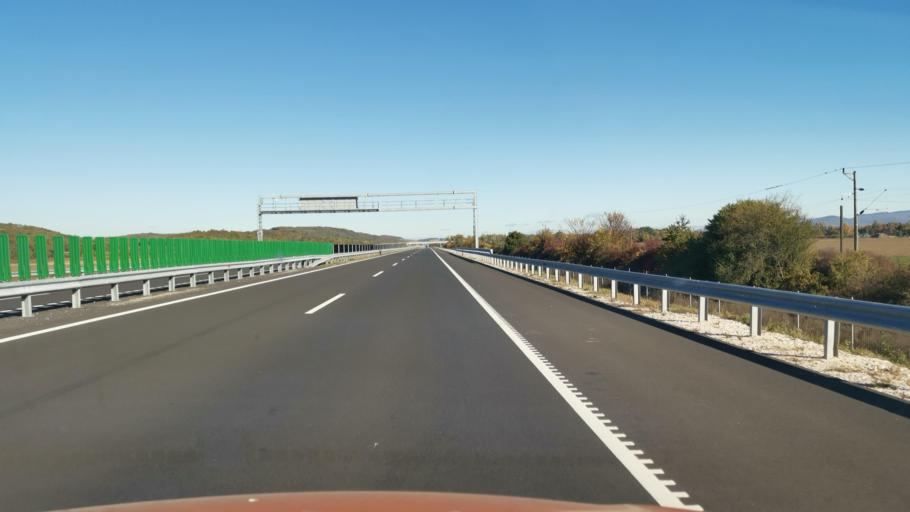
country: HU
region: Borsod-Abauj-Zemplen
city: Gonc
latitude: 48.4367
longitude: 21.1880
